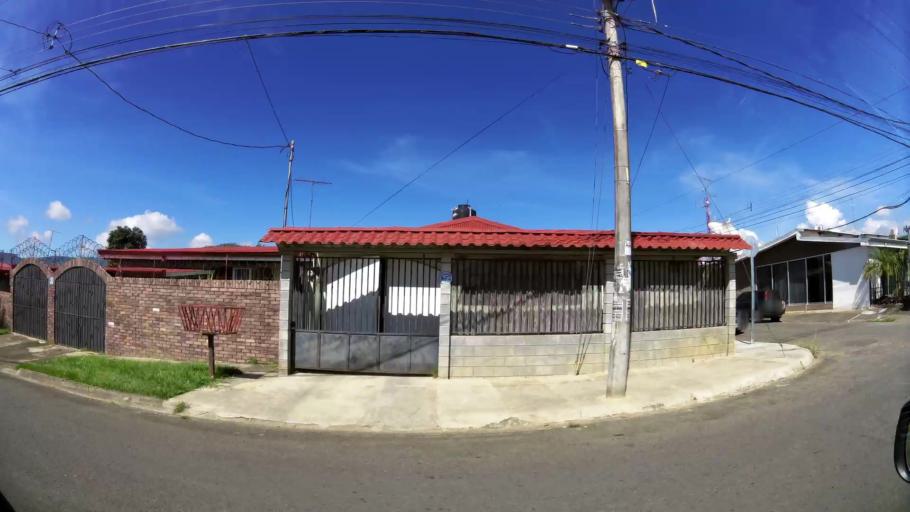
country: CR
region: San Jose
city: San Isidro
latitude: 9.3690
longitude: -83.7123
